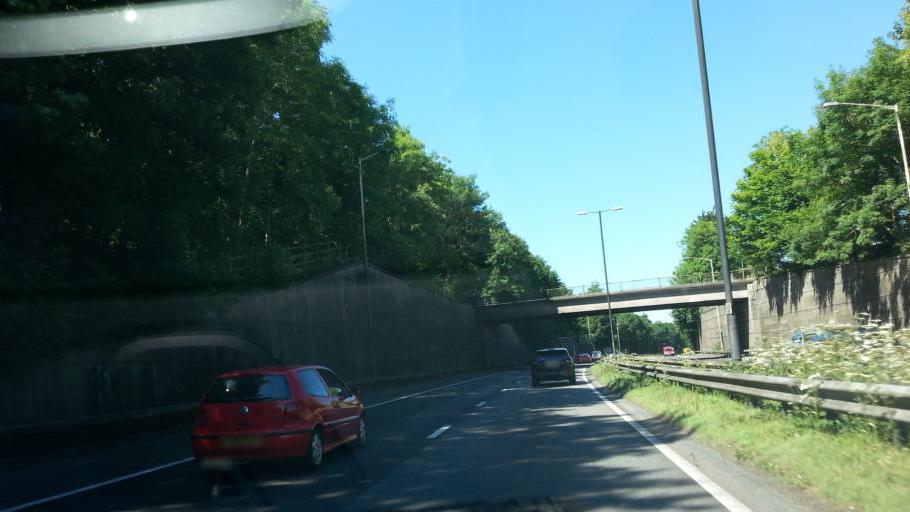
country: GB
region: Wales
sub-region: Newport
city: Marshfield
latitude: 51.5309
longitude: -3.1106
